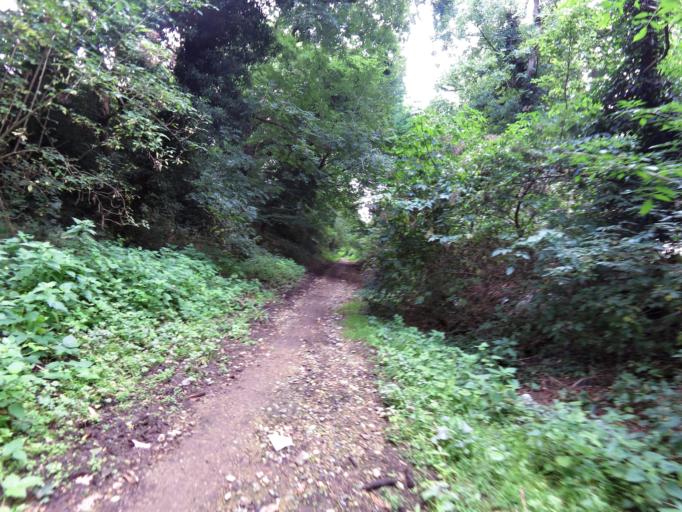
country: GB
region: England
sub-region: Hertfordshire
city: Shenley AV
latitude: 51.7083
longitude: -0.2606
